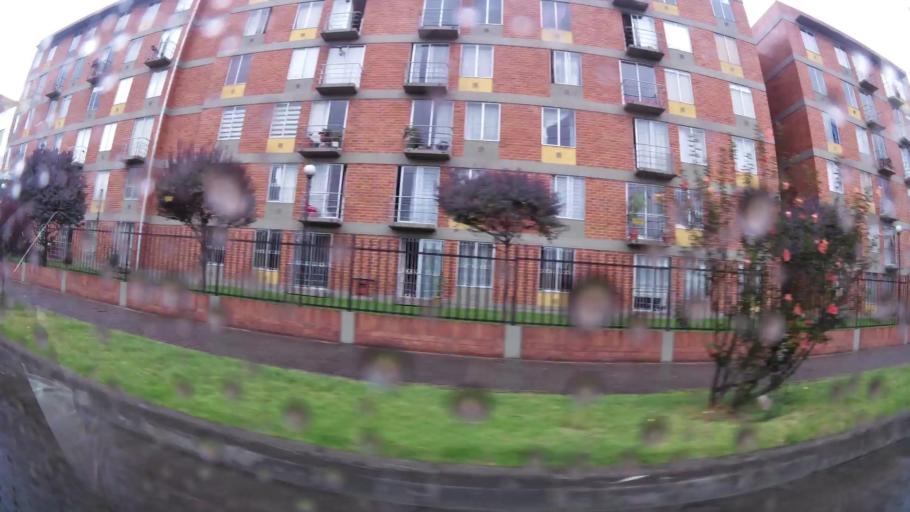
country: CO
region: Bogota D.C.
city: Bogota
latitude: 4.6597
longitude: -74.1308
